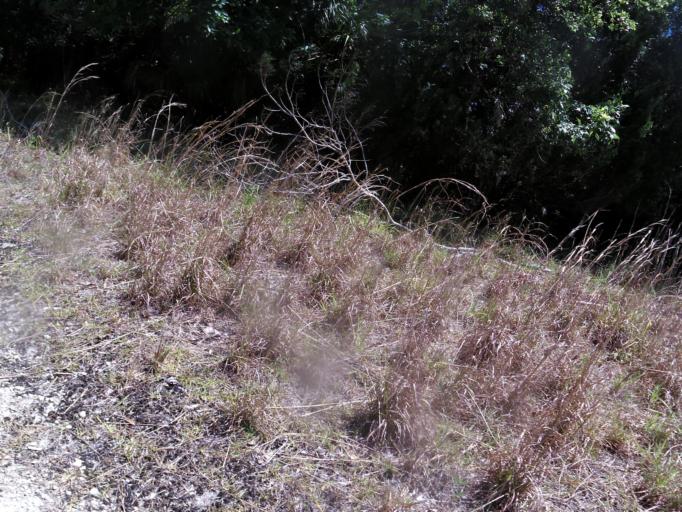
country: US
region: Florida
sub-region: Flagler County
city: Flagler Beach
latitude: 29.4098
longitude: -81.1259
